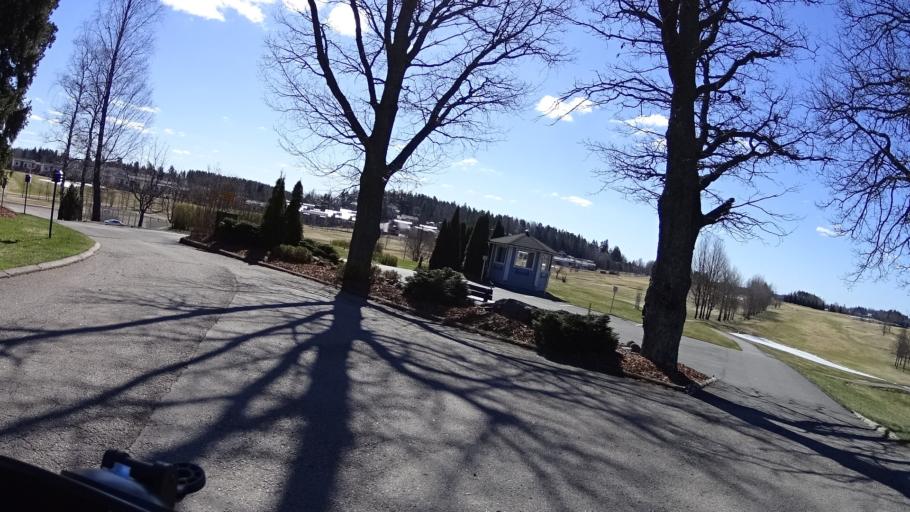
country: FI
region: Uusimaa
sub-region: Helsinki
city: Kauniainen
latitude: 60.2766
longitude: 24.7415
